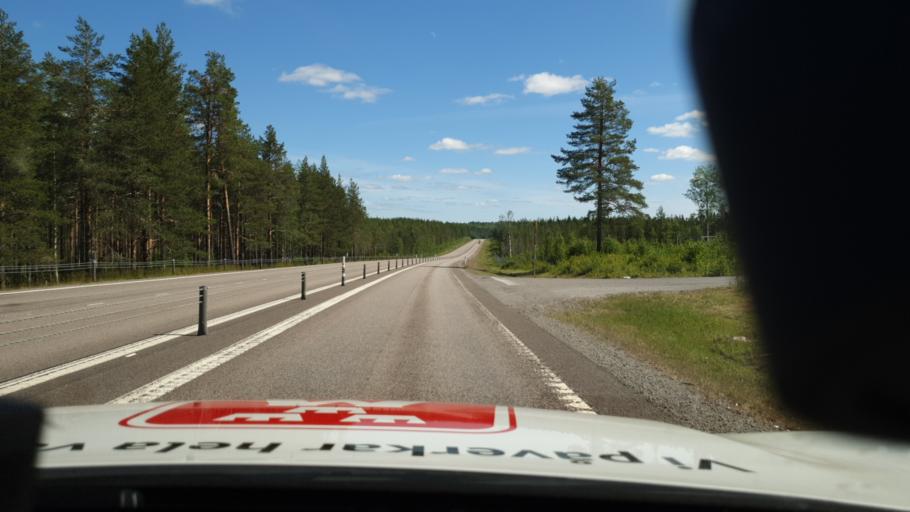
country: SE
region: Norrbotten
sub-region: Kalix Kommun
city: Toere
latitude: 65.9169
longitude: 22.7752
